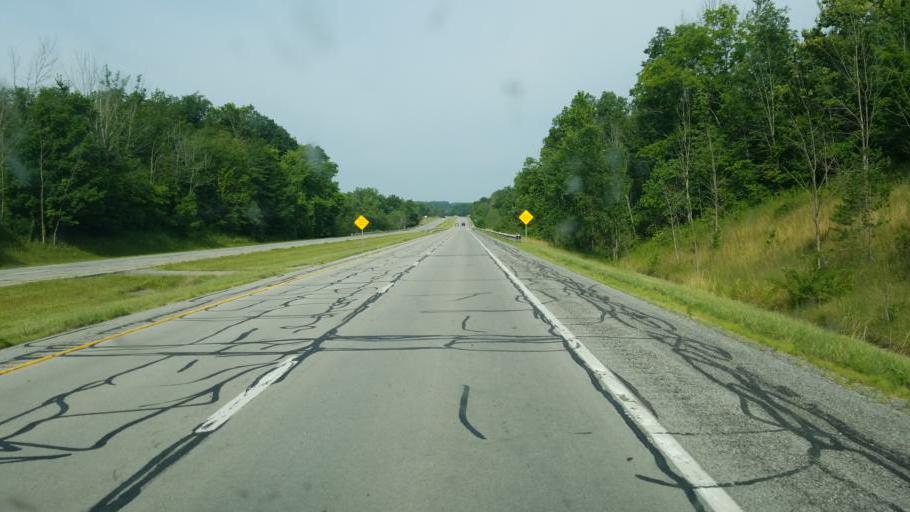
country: US
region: Ohio
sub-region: Medina County
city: Lodi
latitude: 41.0455
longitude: -82.0204
